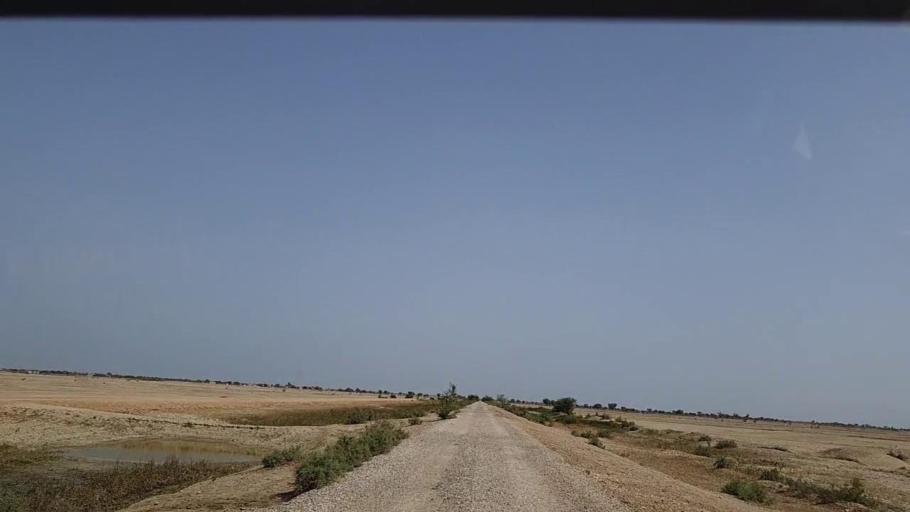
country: PK
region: Sindh
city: Johi
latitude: 26.7624
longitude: 67.6627
